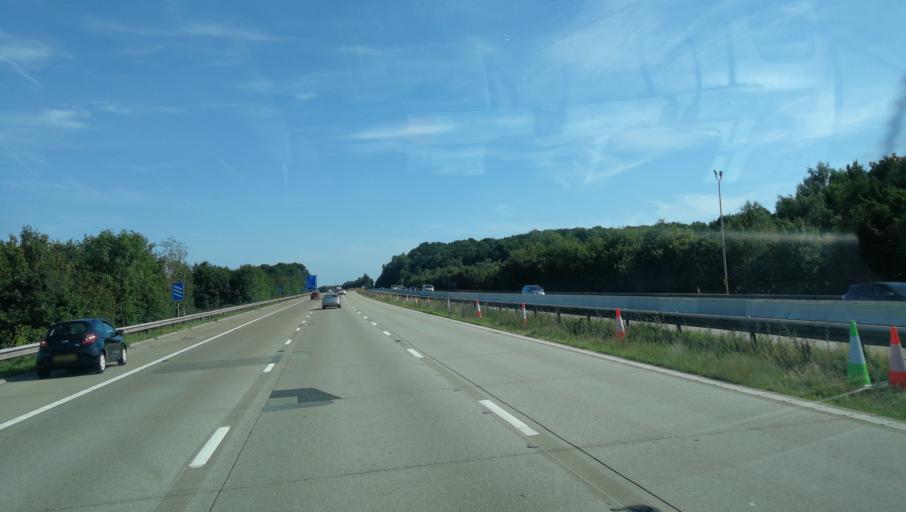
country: GB
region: England
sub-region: Kent
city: Ashford
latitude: 51.1668
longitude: 0.8581
